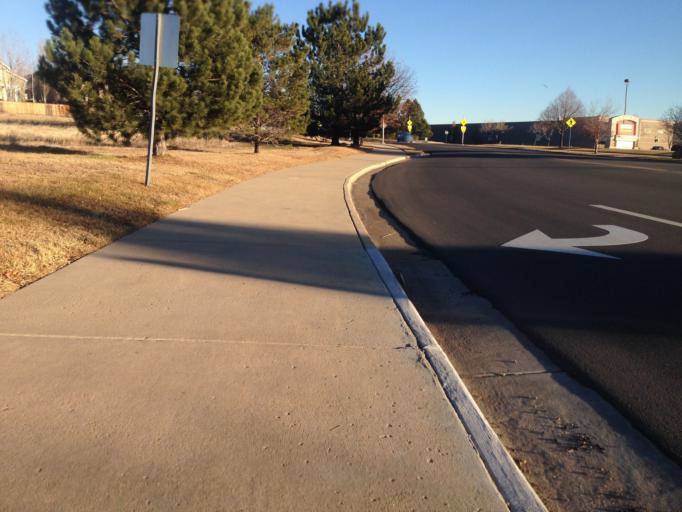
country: US
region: Colorado
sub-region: Broomfield County
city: Broomfield
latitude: 39.9345
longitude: -105.0894
